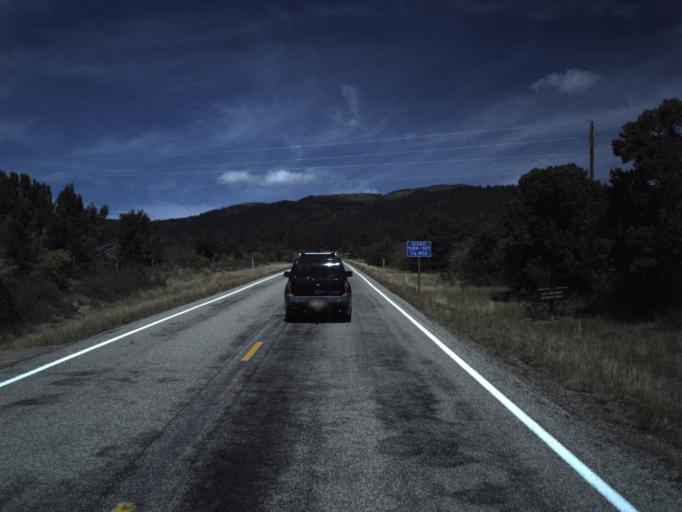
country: US
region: Utah
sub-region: Wayne County
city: Loa
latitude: 37.9782
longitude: -111.4309
